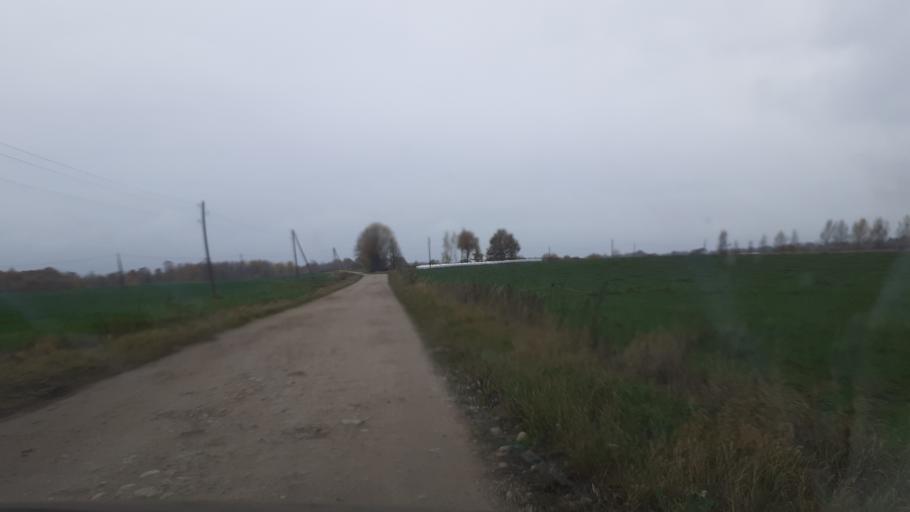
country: LV
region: Saldus Rajons
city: Saldus
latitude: 56.8640
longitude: 22.3496
